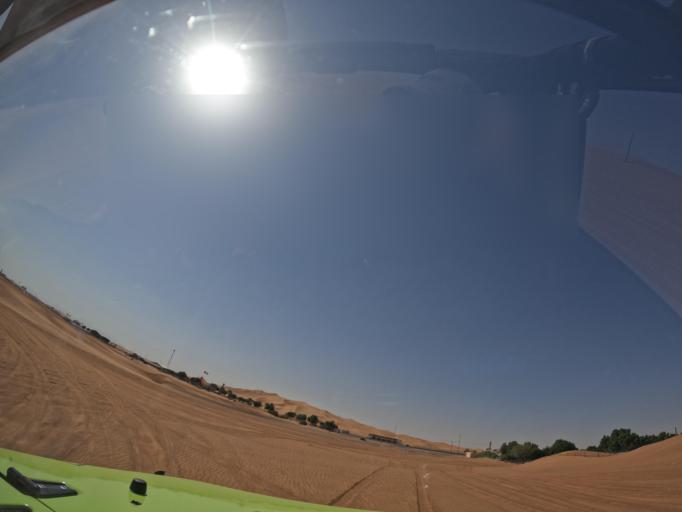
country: AE
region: Ash Shariqah
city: Adh Dhayd
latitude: 24.9567
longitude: 55.7164
